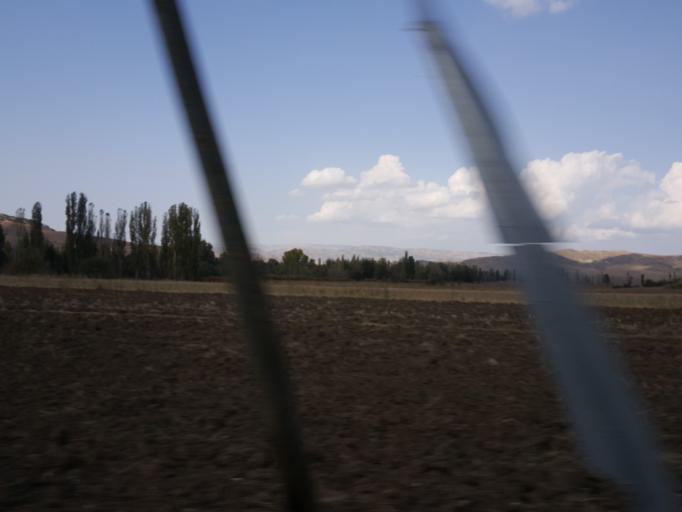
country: TR
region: Corum
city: Bogazkale
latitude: 40.1293
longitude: 34.5371
